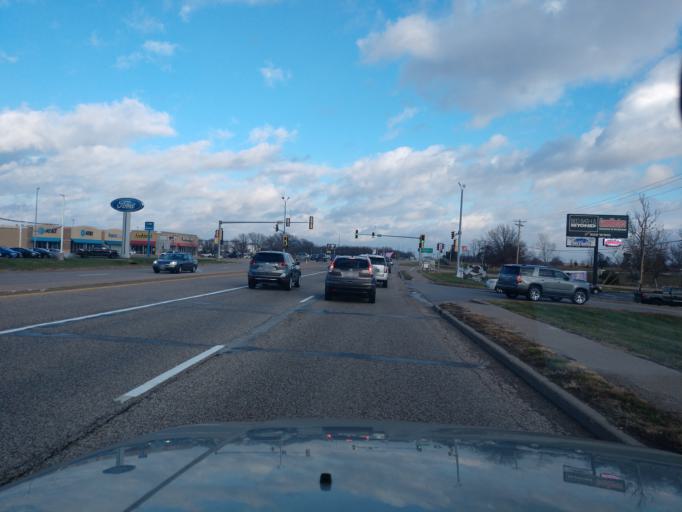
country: US
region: Illinois
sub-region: Adams County
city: Quincy
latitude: 39.9351
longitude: -91.3350
